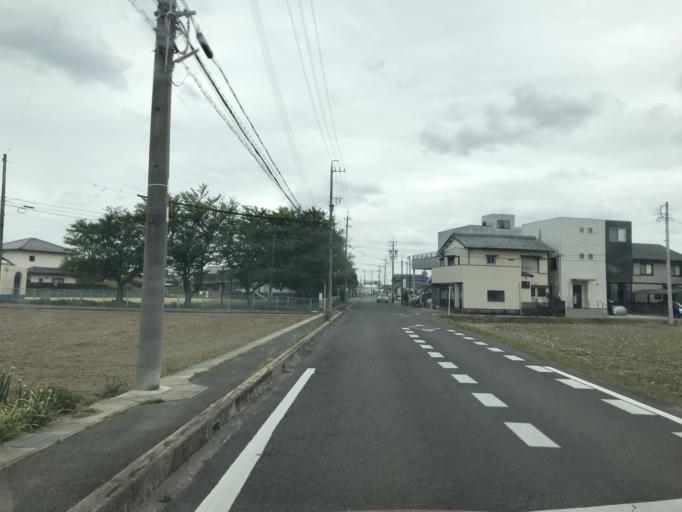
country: JP
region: Aichi
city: Kasugai
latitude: 35.2666
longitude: 136.9687
